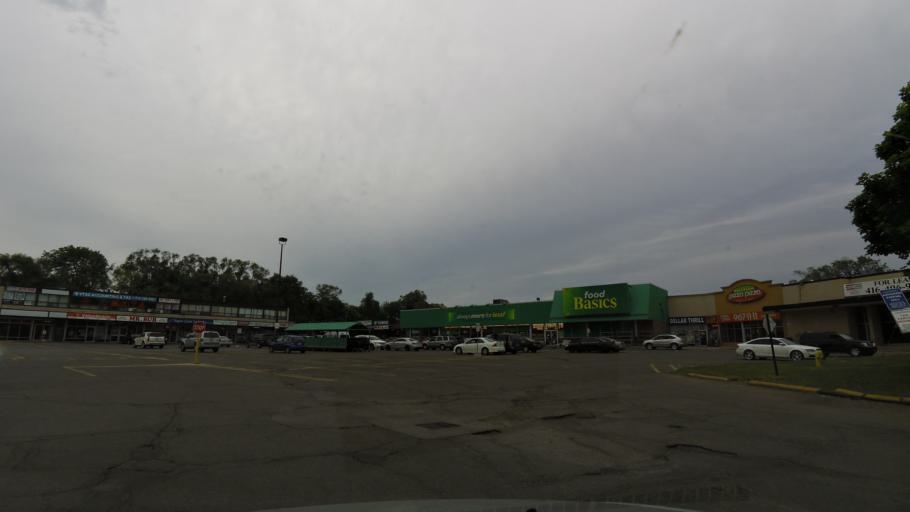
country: CA
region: Ontario
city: Etobicoke
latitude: 43.6763
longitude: -79.4950
